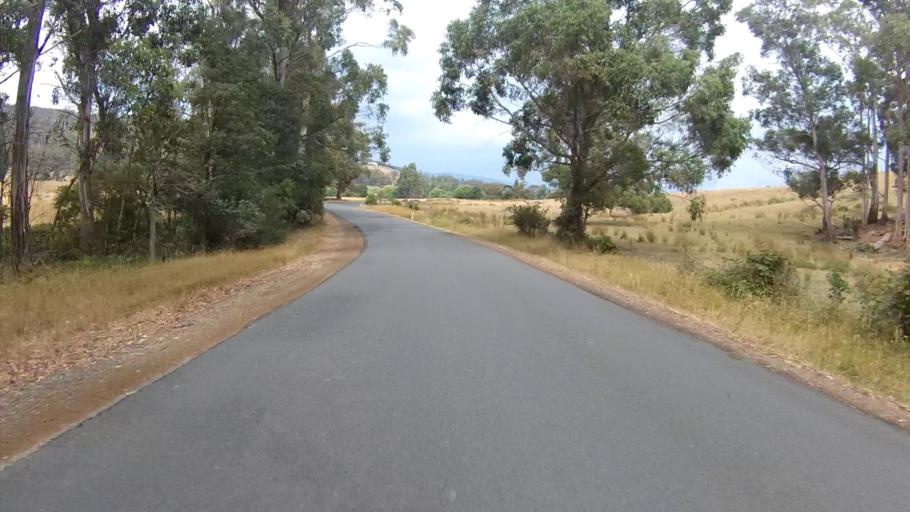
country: AU
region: Tasmania
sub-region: Huon Valley
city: Cygnet
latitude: -43.1817
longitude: 147.1125
